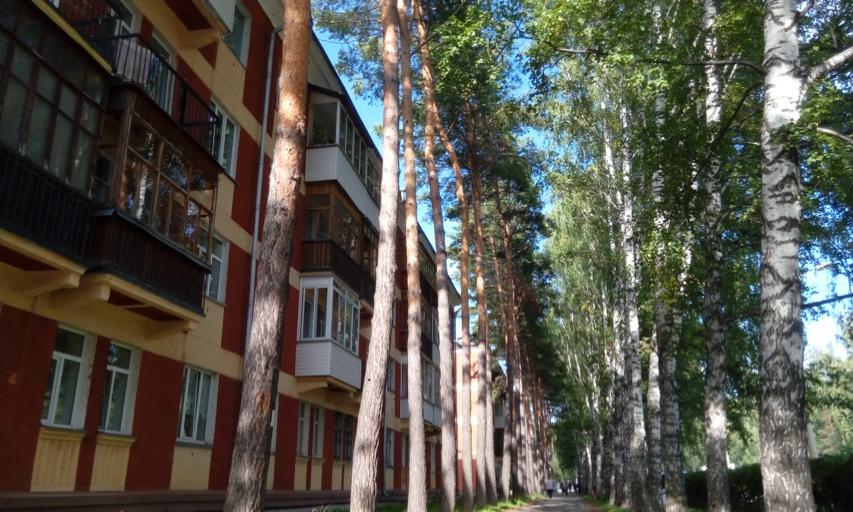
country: RU
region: Novosibirsk
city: Akademgorodok
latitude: 54.8355
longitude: 83.0982
